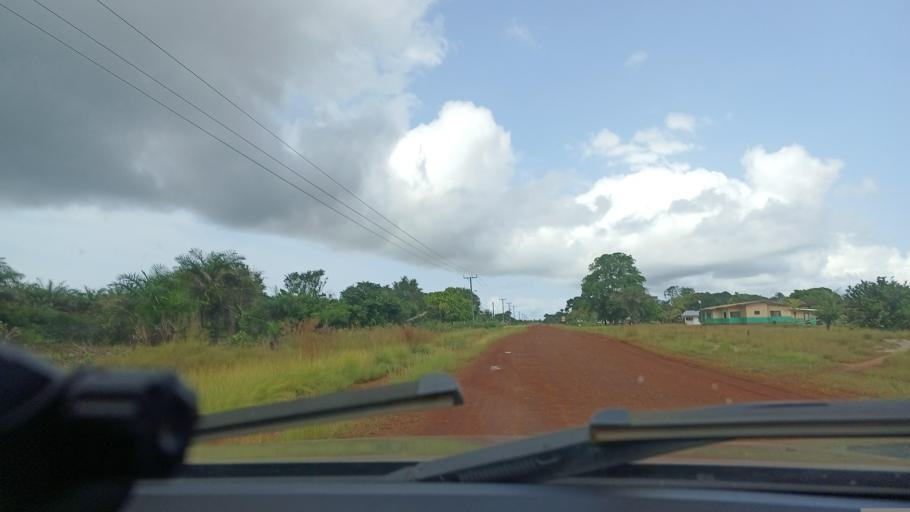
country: LR
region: Grand Cape Mount
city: Robertsport
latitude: 6.6913
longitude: -11.2657
